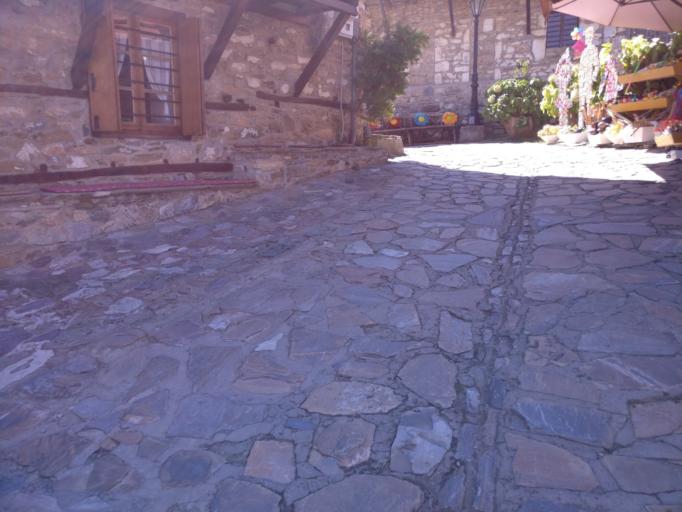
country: GR
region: Central Macedonia
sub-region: Nomos Pierias
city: Leptokarya
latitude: 39.9916
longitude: 22.5705
